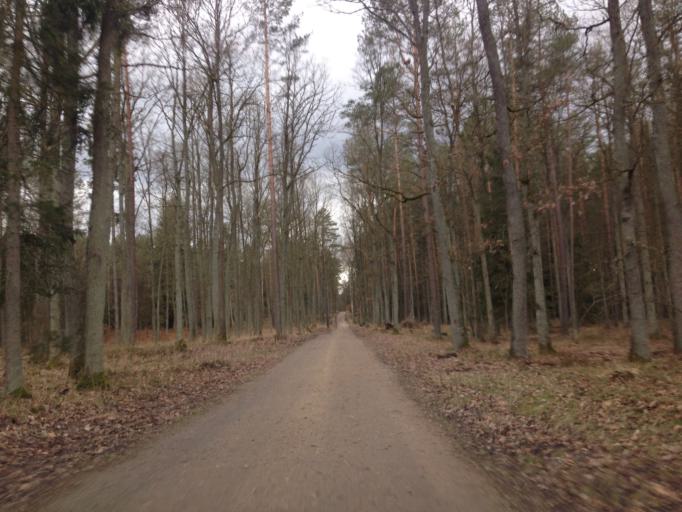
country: PL
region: Kujawsko-Pomorskie
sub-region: Powiat brodnicki
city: Gorzno
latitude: 53.1763
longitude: 19.6984
